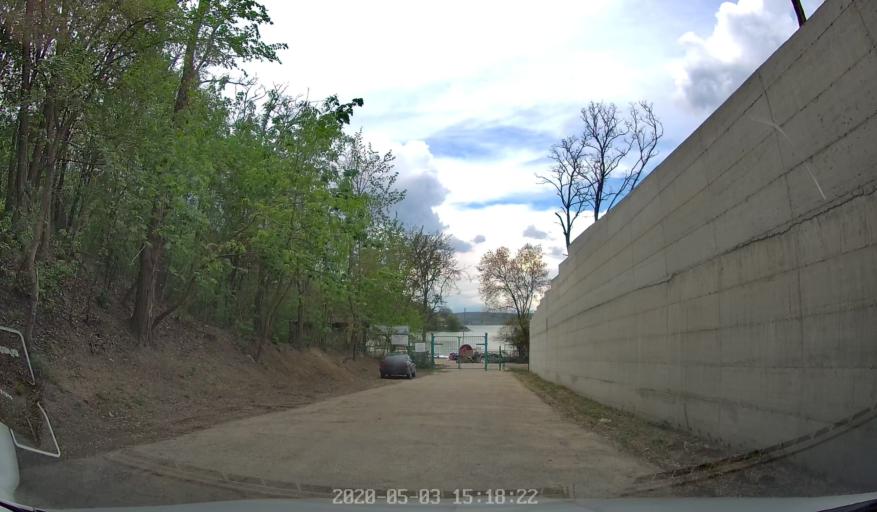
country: MD
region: Chisinau
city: Vatra
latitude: 47.0865
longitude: 28.7138
